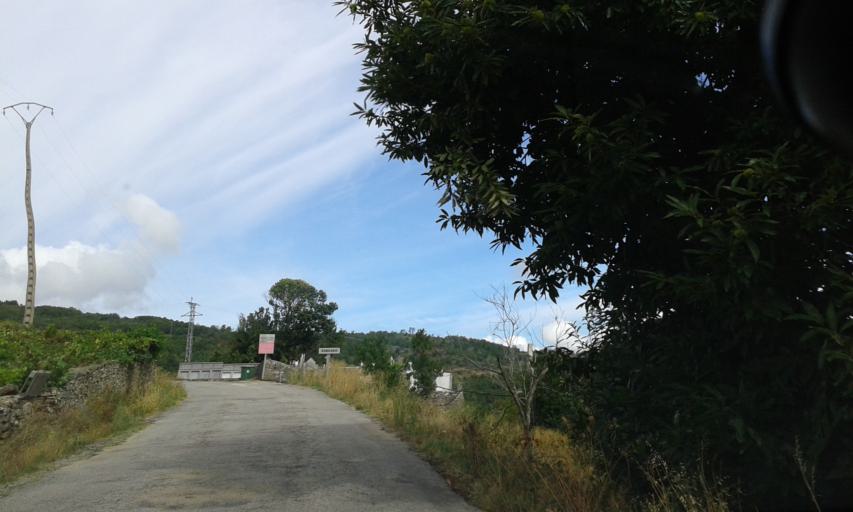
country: ES
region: Galicia
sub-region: Provincia de Ourense
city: Manzaneda
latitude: 42.3146
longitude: -7.2369
